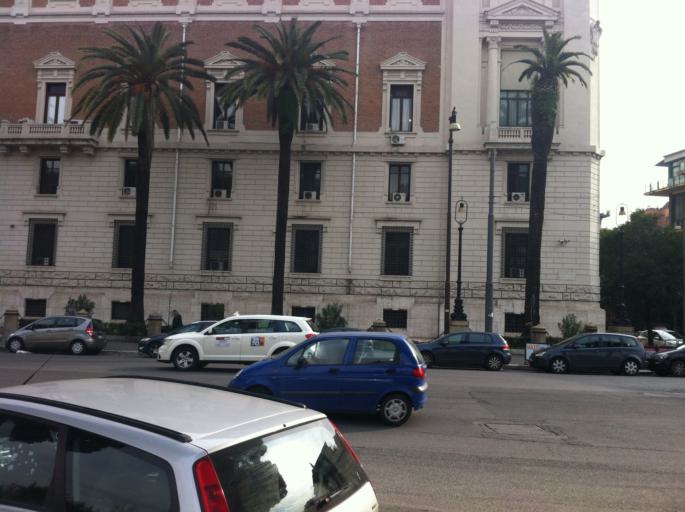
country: VA
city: Vatican City
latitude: 41.9148
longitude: 12.4715
